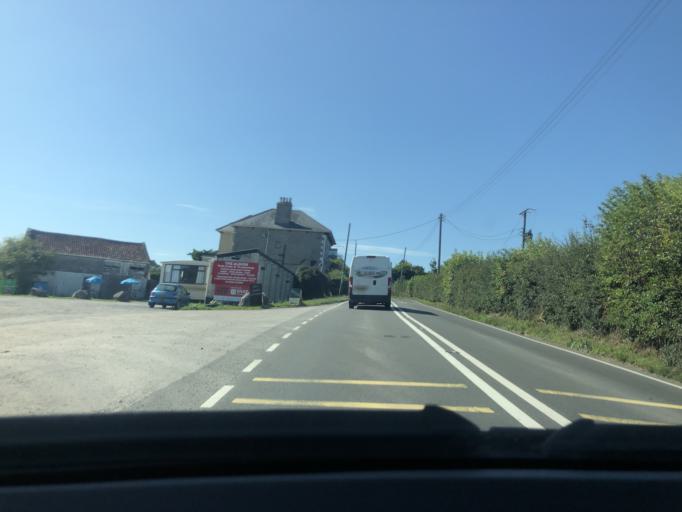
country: GB
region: England
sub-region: Somerset
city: Street
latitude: 51.1314
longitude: -2.8244
